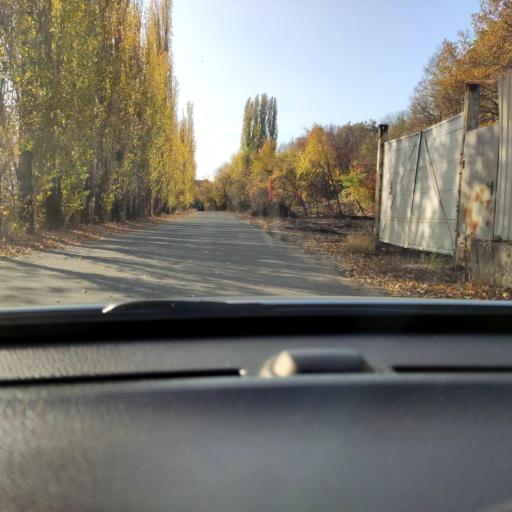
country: RU
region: Voronezj
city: Voronezh
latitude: 51.7029
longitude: 39.2372
